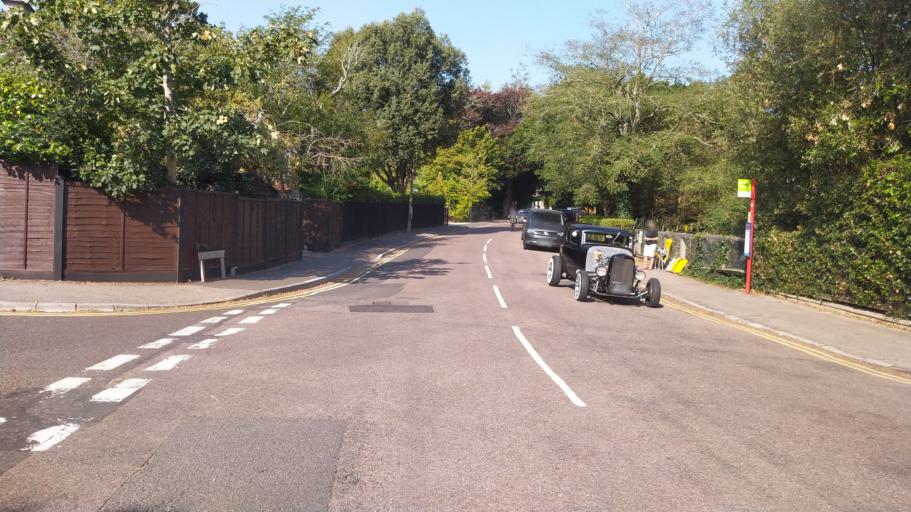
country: GB
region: England
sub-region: Dorset
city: Parkstone
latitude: 50.7024
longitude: -1.9225
